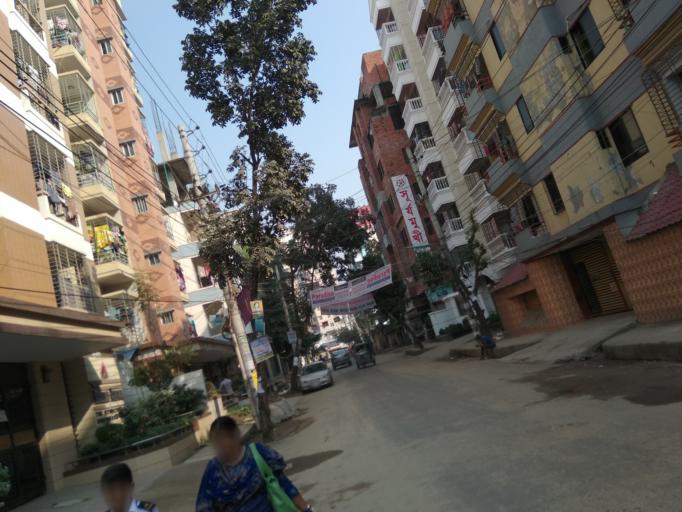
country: BD
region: Dhaka
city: Tungi
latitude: 23.8264
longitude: 90.3627
